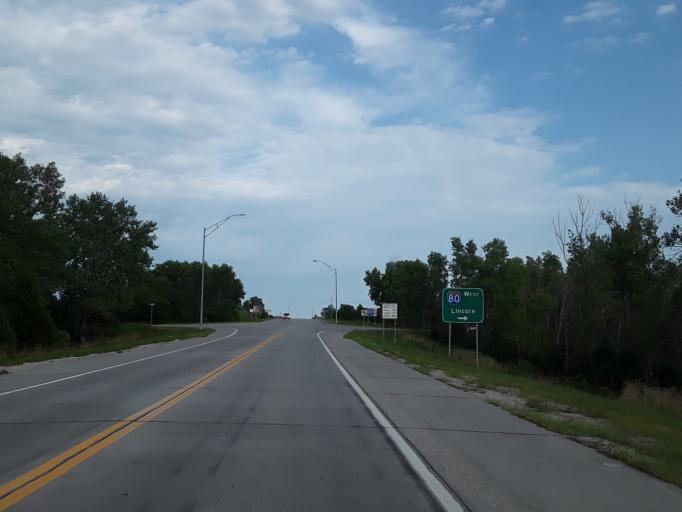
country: US
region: Nebraska
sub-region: Saunders County
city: Ashland
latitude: 41.0137
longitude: -96.3109
